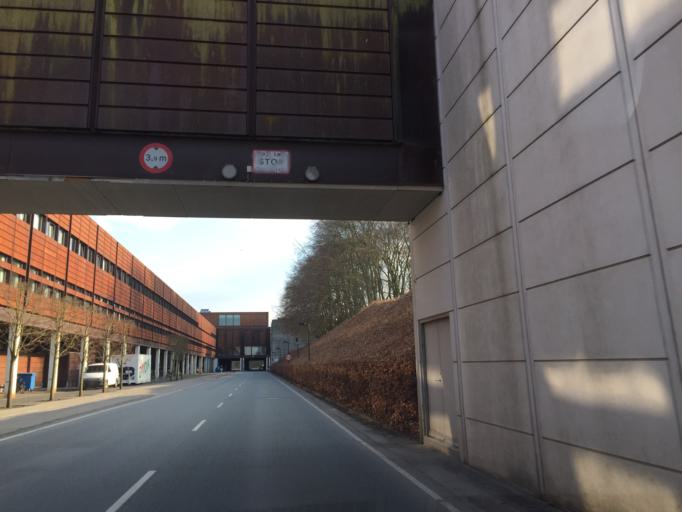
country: DK
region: South Denmark
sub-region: Odense Kommune
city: Neder Holluf
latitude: 55.3698
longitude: 10.4277
